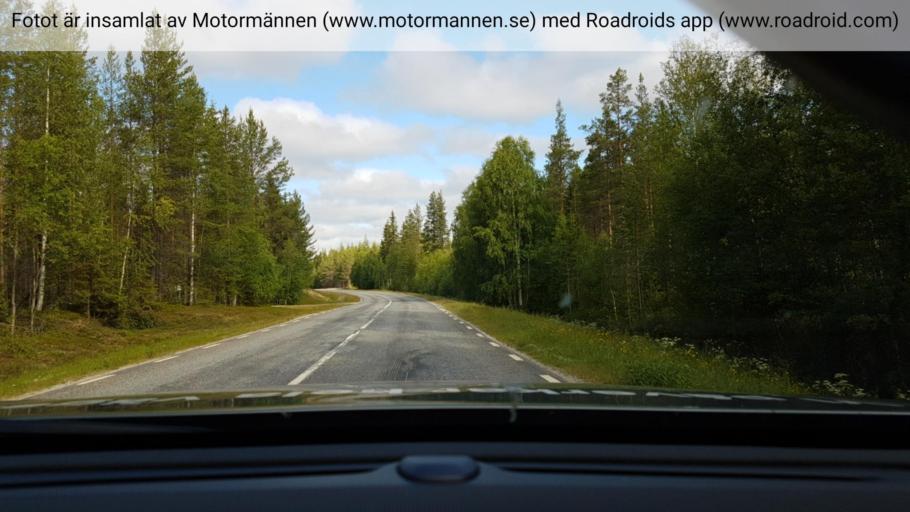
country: SE
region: Vaesterbotten
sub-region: Lycksele Kommun
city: Lycksele
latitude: 64.7924
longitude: 18.9736
